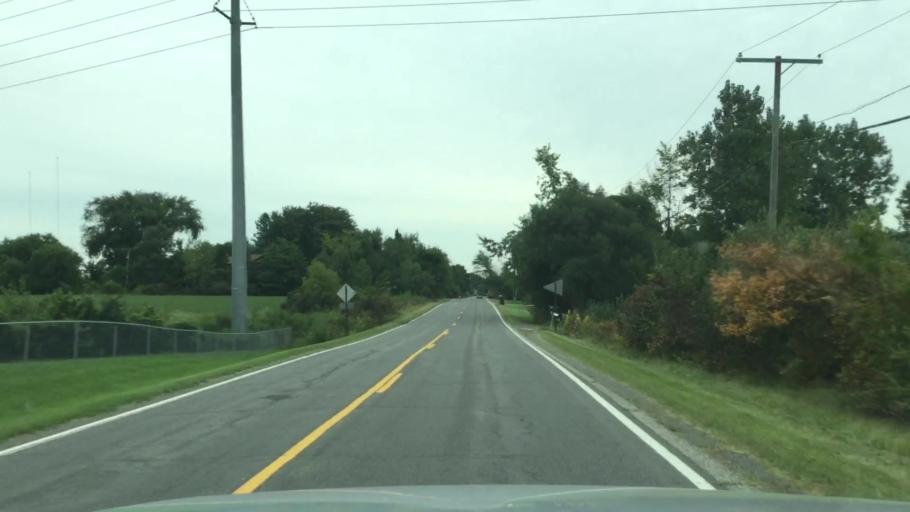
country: US
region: Michigan
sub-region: Washtenaw County
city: Milan
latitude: 42.1425
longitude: -83.6623
